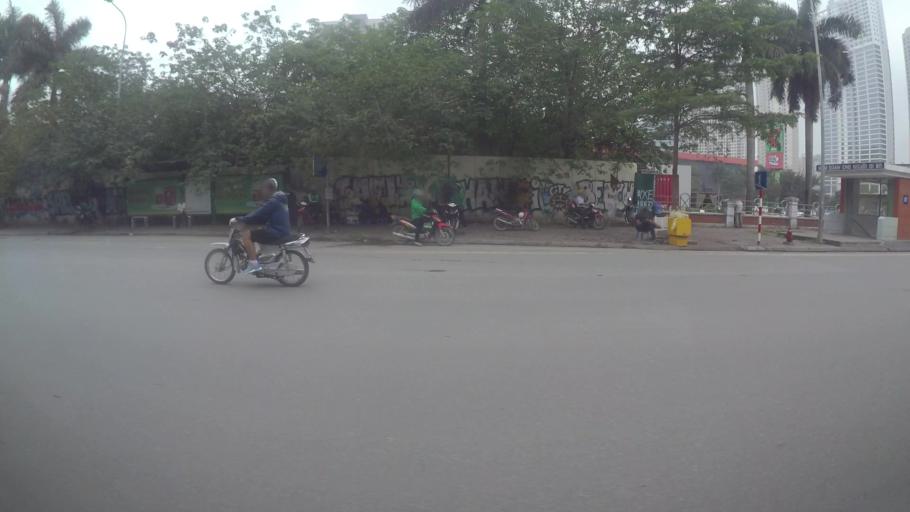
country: VN
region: Ha Noi
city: Thanh Xuan
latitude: 21.0068
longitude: 105.7912
